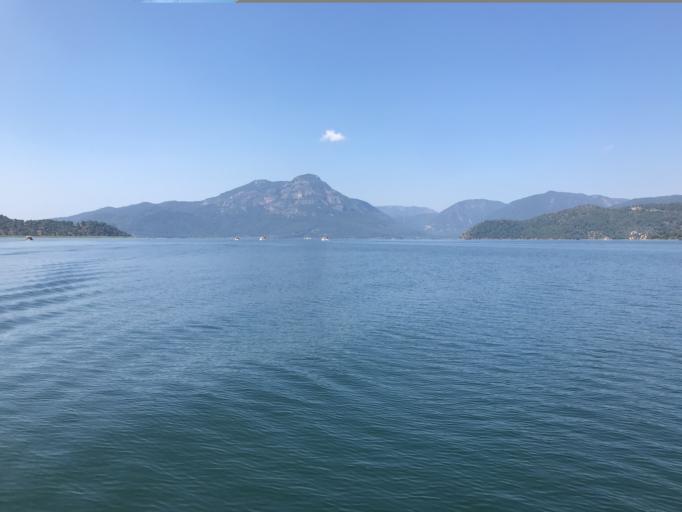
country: TR
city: Dalyan
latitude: 36.9118
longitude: 28.6540
